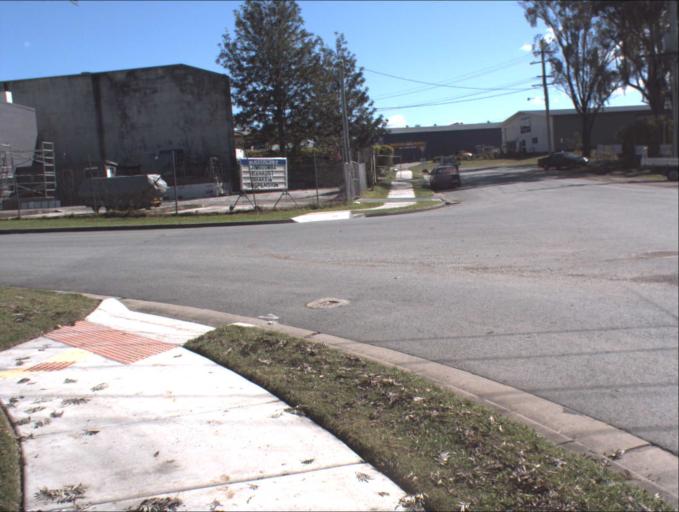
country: AU
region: Queensland
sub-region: Logan
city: North Maclean
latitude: -27.8239
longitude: 153.0315
